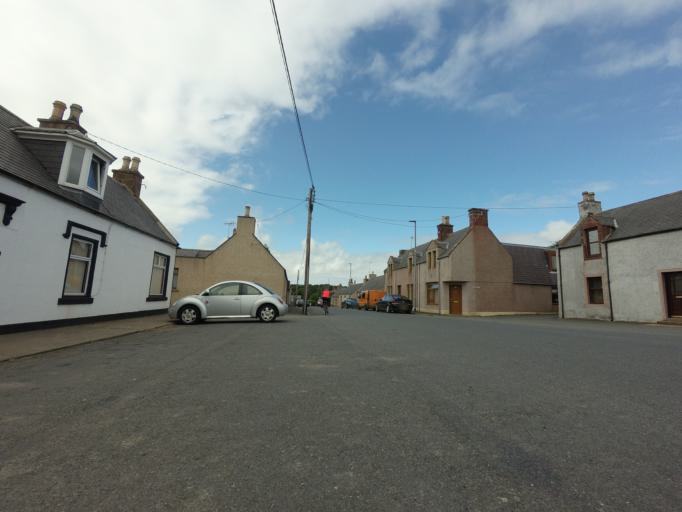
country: GB
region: Scotland
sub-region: Aberdeenshire
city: Turriff
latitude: 57.5426
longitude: -2.3352
